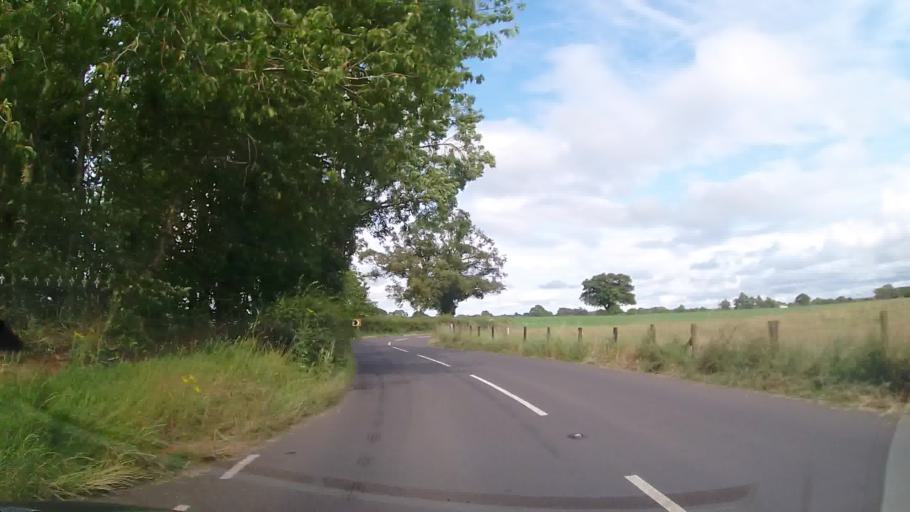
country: GB
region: England
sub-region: Shropshire
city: Petton
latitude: 52.8620
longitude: -2.7834
